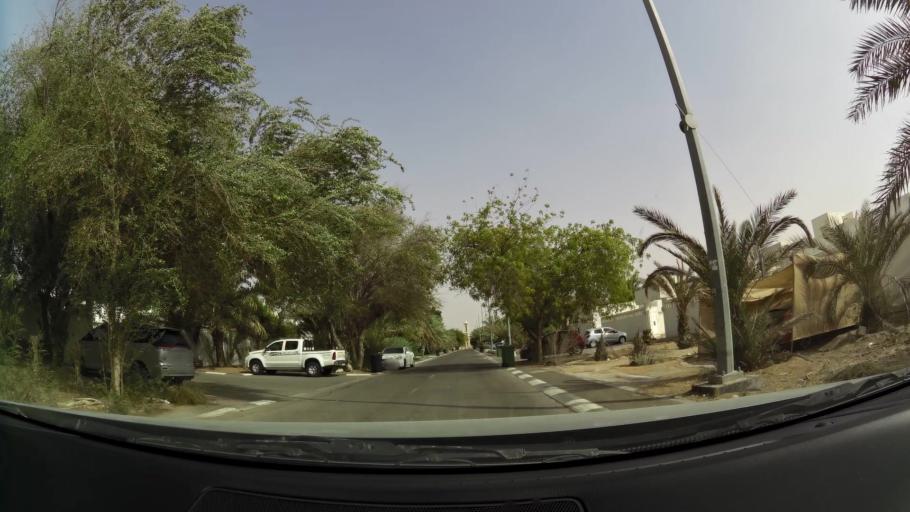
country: AE
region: Abu Dhabi
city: Al Ain
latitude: 24.1808
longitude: 55.6027
